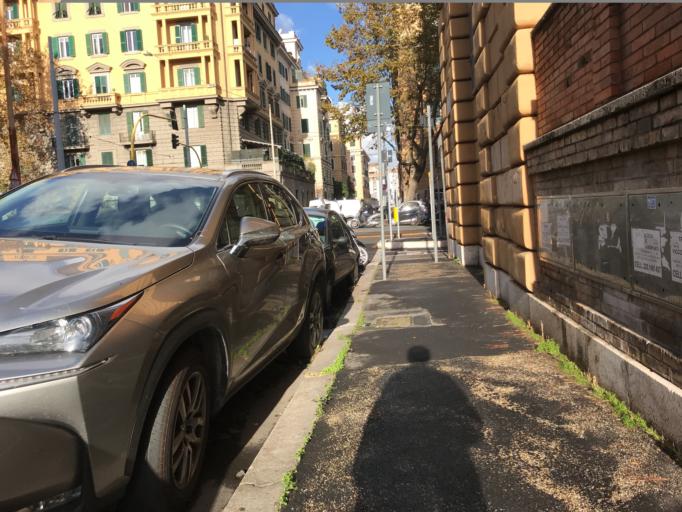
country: IT
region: Latium
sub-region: Citta metropolitana di Roma Capitale
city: Rome
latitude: 41.9118
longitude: 12.5057
